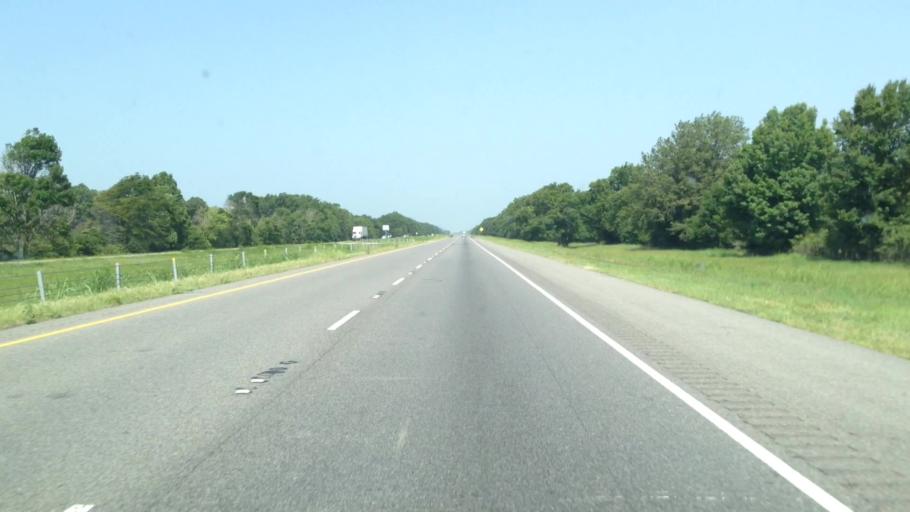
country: US
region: Louisiana
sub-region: Madison Parish
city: Tallulah
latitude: 32.4074
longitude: -91.2379
